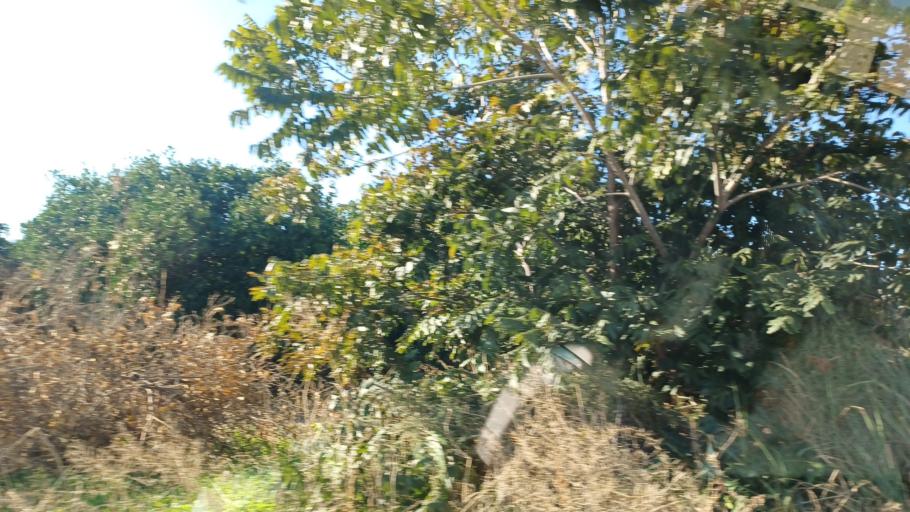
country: CY
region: Pafos
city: Polis
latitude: 35.0161
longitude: 32.4321
